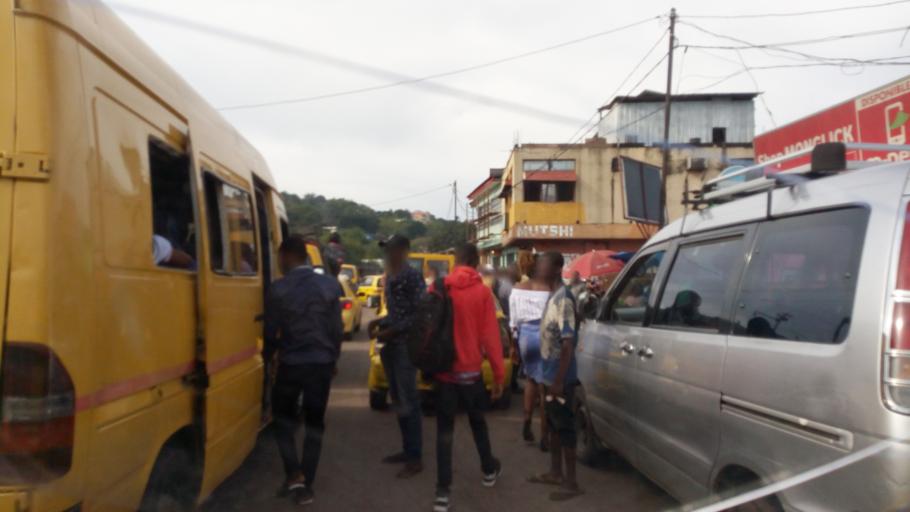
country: CD
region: Kinshasa
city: Kinshasa
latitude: -4.4255
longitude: 15.2578
